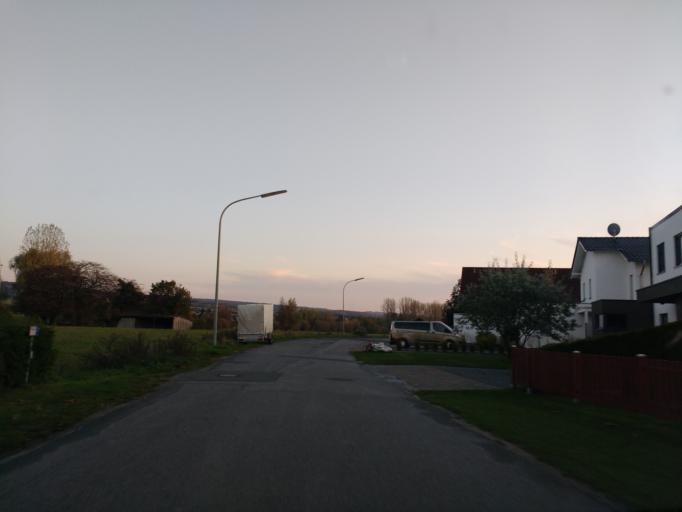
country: DE
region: North Rhine-Westphalia
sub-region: Regierungsbezirk Detmold
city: Schlangen
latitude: 51.8029
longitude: 8.8424
